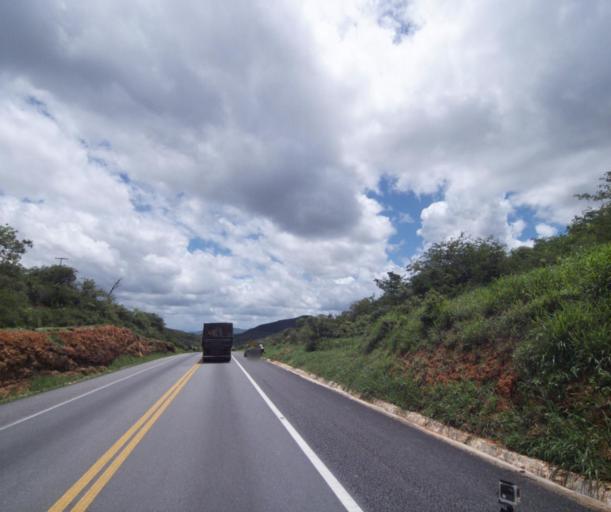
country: BR
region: Bahia
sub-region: Pocoes
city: Pocoes
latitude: -14.3654
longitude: -40.3440
